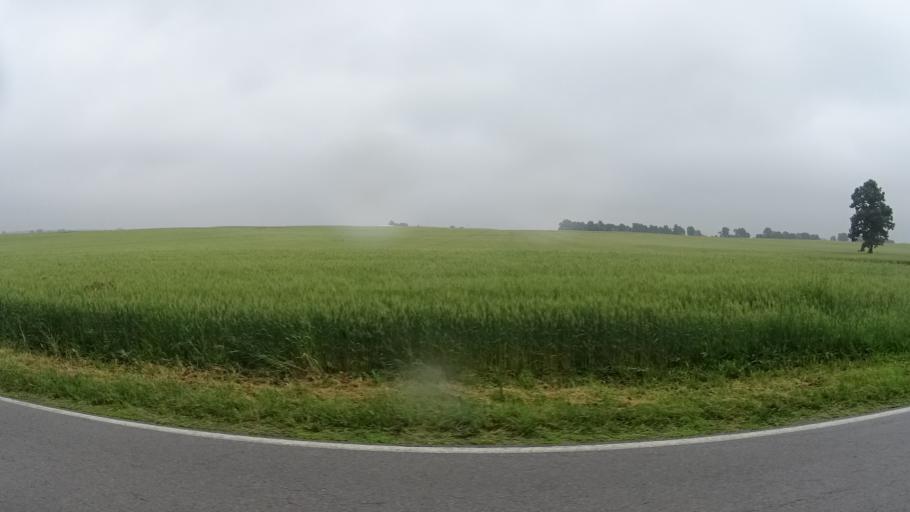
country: US
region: Ohio
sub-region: Huron County
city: Bellevue
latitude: 41.3111
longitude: -82.8424
